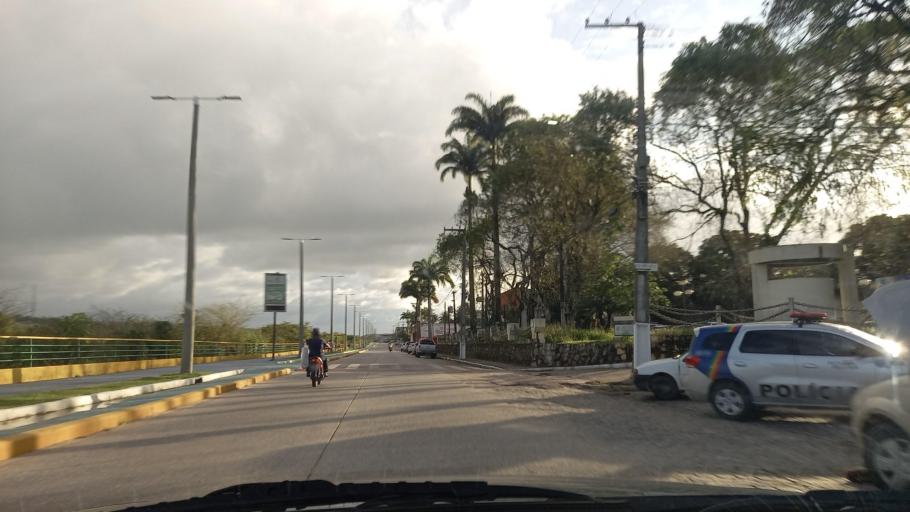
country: BR
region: Pernambuco
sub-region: Palmares
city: Palmares
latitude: -8.6793
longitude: -35.5792
